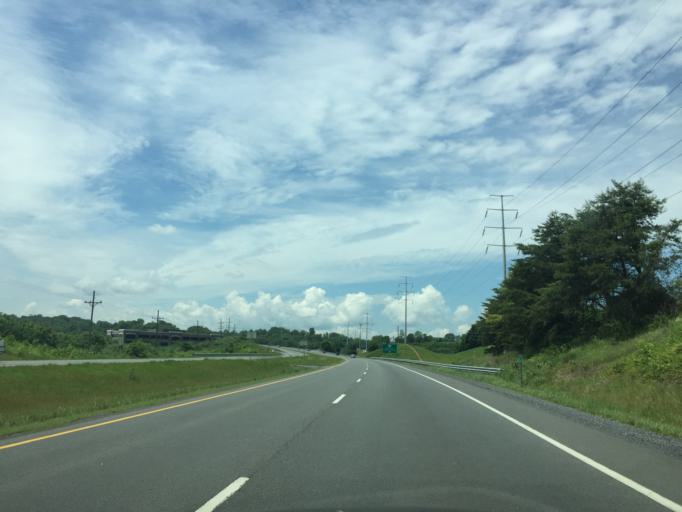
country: US
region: Virginia
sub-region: City of Winchester
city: Winchester
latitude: 39.2130
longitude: -78.1724
